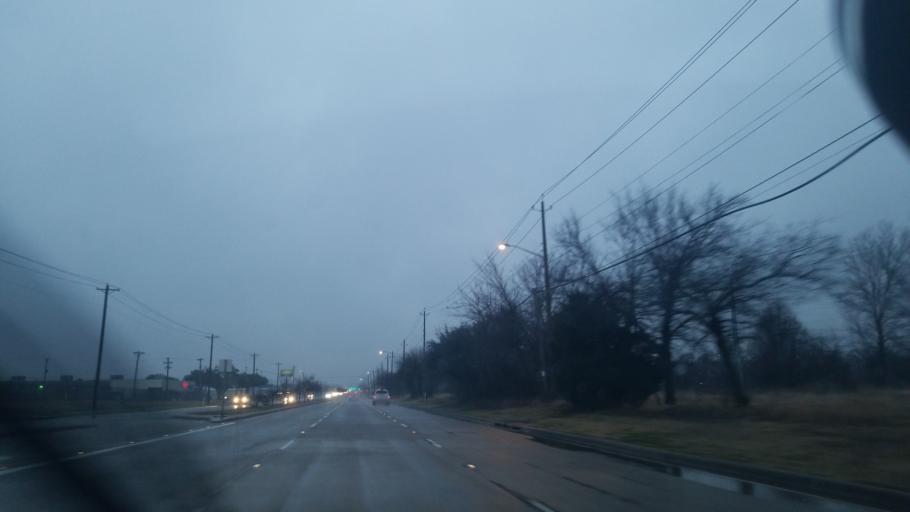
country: US
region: Texas
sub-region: Denton County
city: Denton
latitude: 33.2225
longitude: -97.0905
